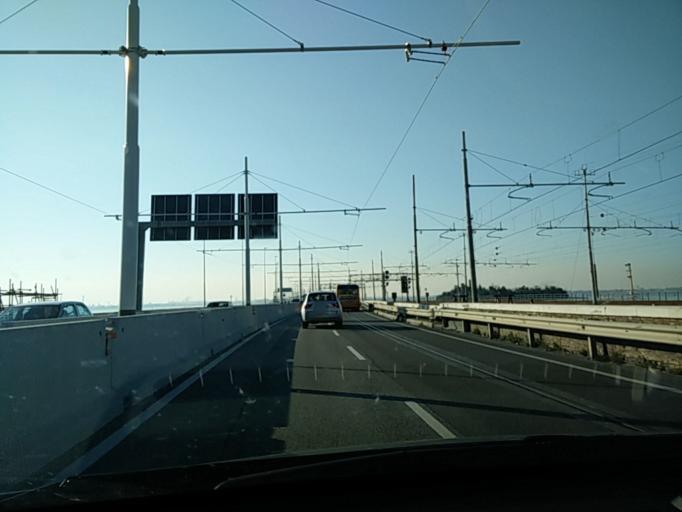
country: IT
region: Veneto
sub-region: Provincia di Venezia
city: Venice
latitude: 45.4467
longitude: 12.3111
